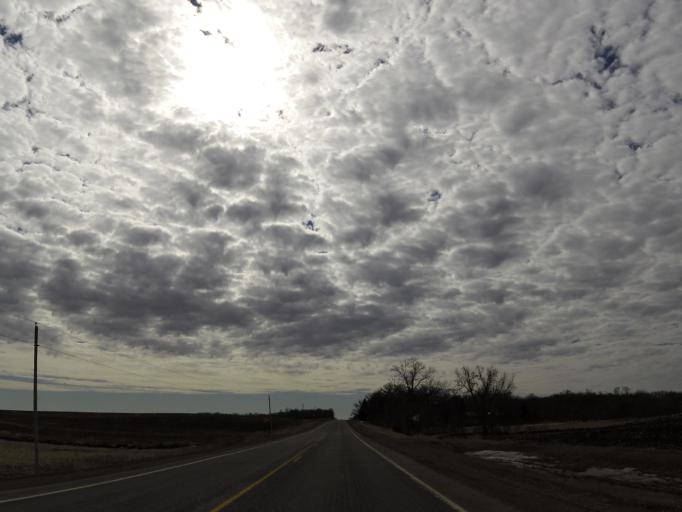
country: US
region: Minnesota
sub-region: Scott County
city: Shakopee
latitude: 44.7010
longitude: -93.5210
